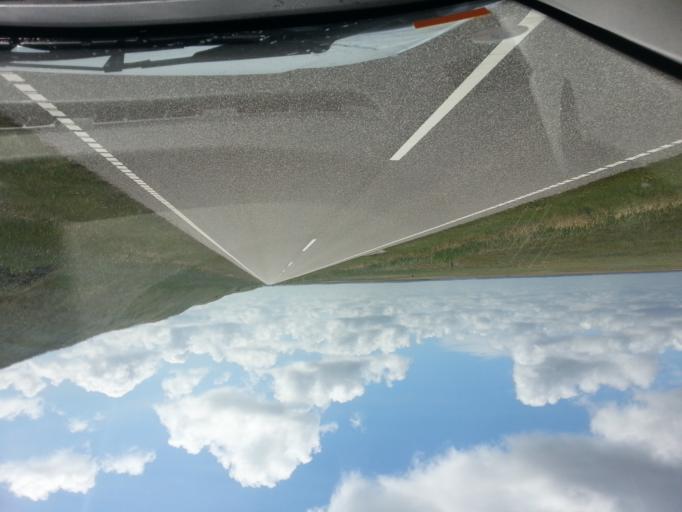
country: DK
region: Central Jutland
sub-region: Lemvig Kommune
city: Harboore
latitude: 56.4215
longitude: 8.1233
